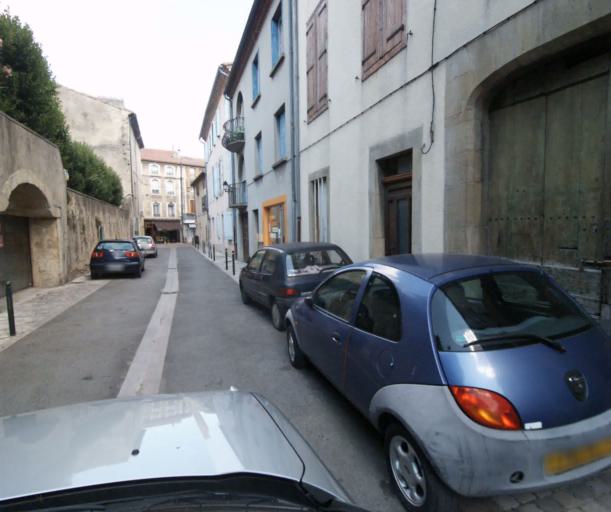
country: FR
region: Languedoc-Roussillon
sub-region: Departement de l'Aude
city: Limoux
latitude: 43.0544
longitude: 2.2158
